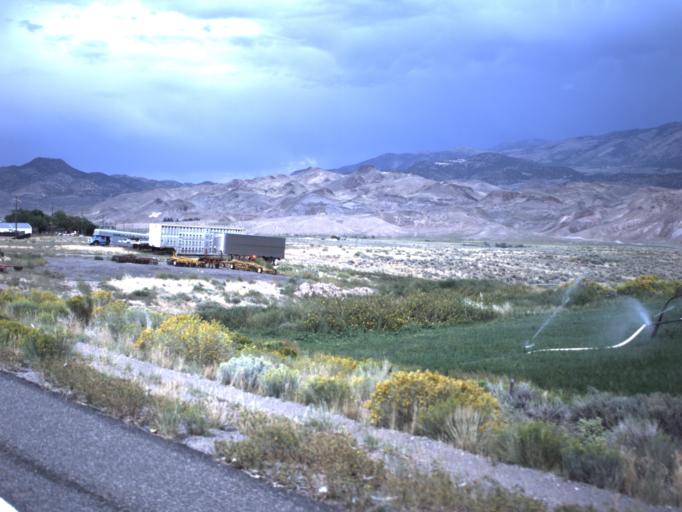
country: US
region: Utah
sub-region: Piute County
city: Junction
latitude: 38.4283
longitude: -112.2317
